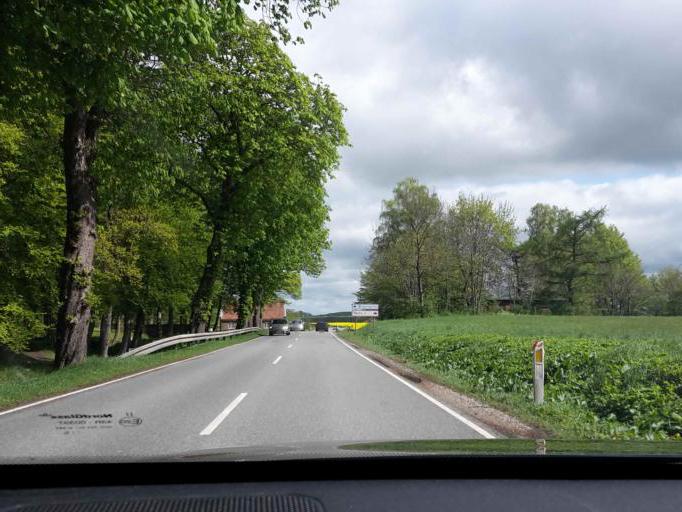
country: DK
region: Central Jutland
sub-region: Syddjurs Kommune
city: Hornslet
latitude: 56.3319
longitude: 10.3322
